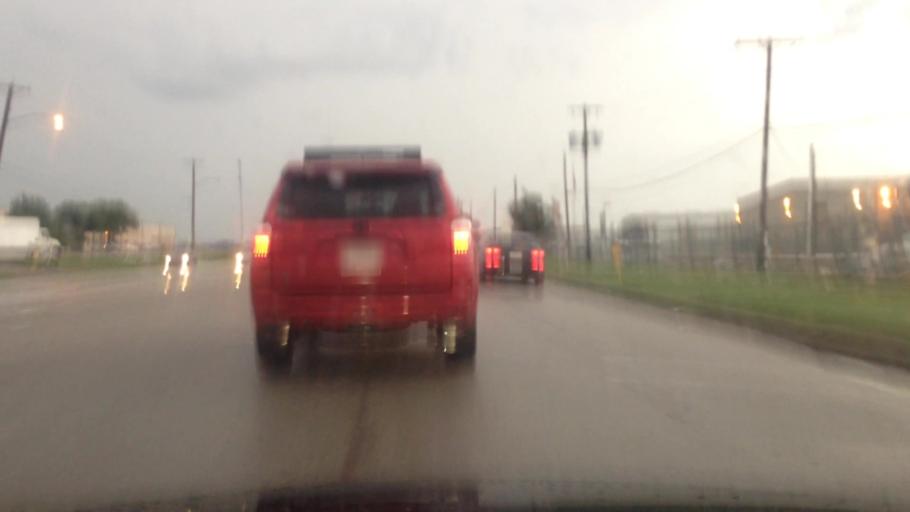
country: US
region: Texas
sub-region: Tarrant County
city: Blue Mound
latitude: 32.8248
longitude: -97.3426
